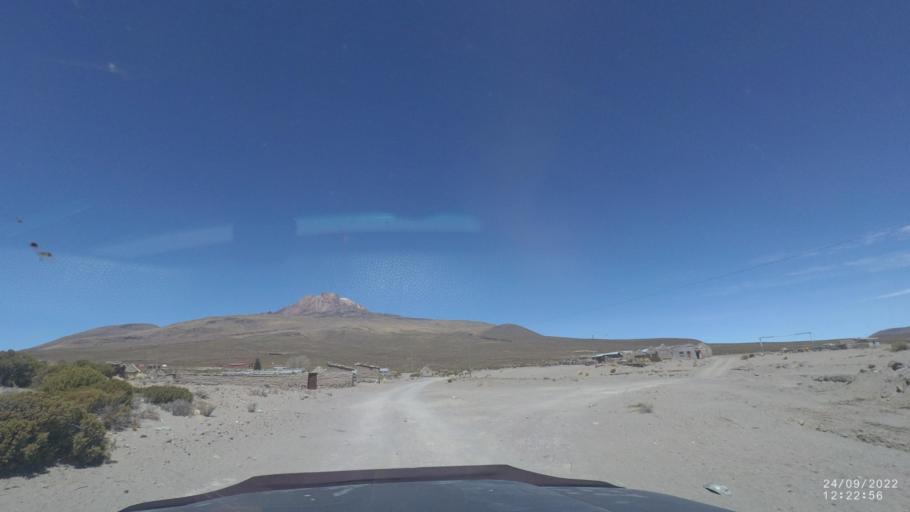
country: BO
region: Potosi
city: Colchani
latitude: -19.7603
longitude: -67.6644
